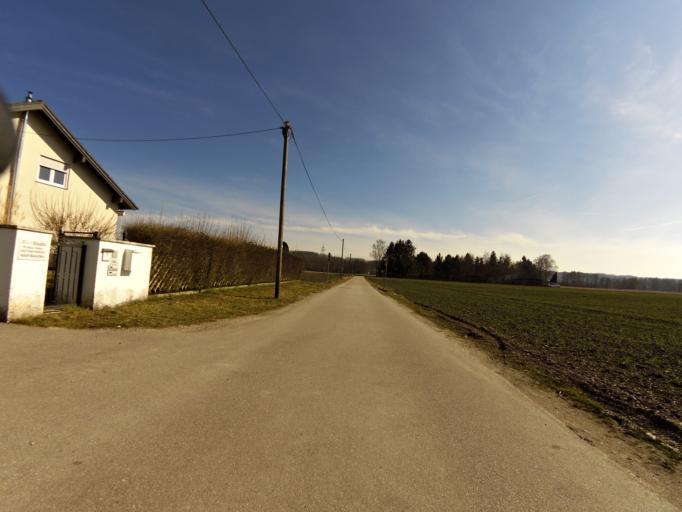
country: DE
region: Bavaria
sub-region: Lower Bavaria
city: Bruckberg
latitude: 48.4970
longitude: 12.0185
